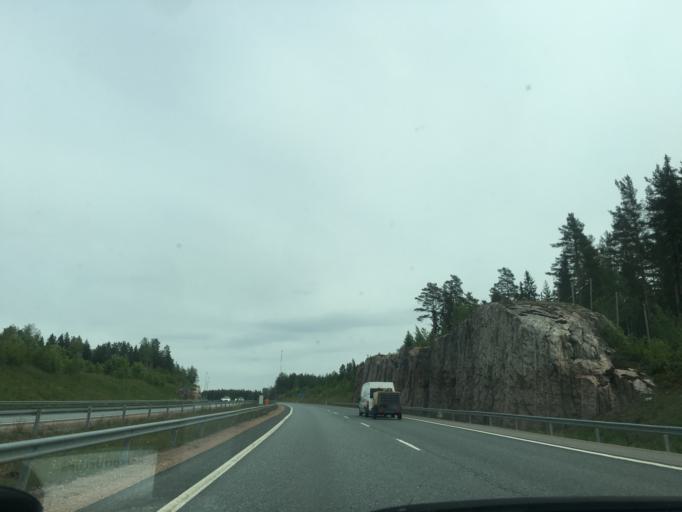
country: FI
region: Varsinais-Suomi
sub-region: Salo
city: Suomusjaervi
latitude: 60.3683
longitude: 23.6943
